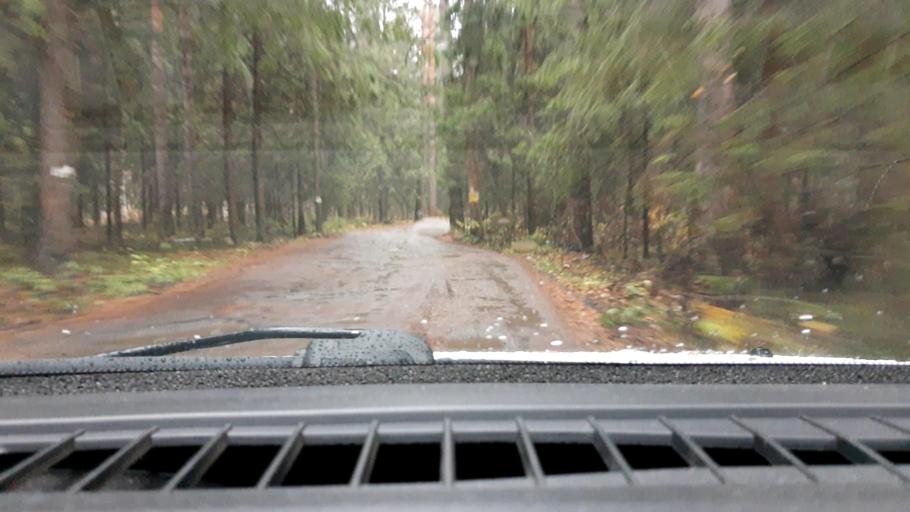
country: RU
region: Nizjnij Novgorod
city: Linda
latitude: 56.6784
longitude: 44.1914
